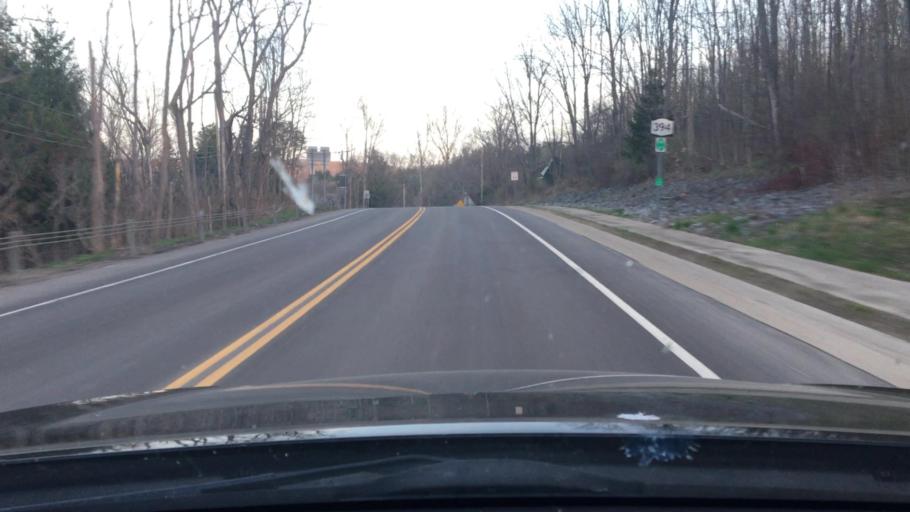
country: US
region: New York
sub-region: Cattaraugus County
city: Randolph
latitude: 42.1713
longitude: -78.9400
